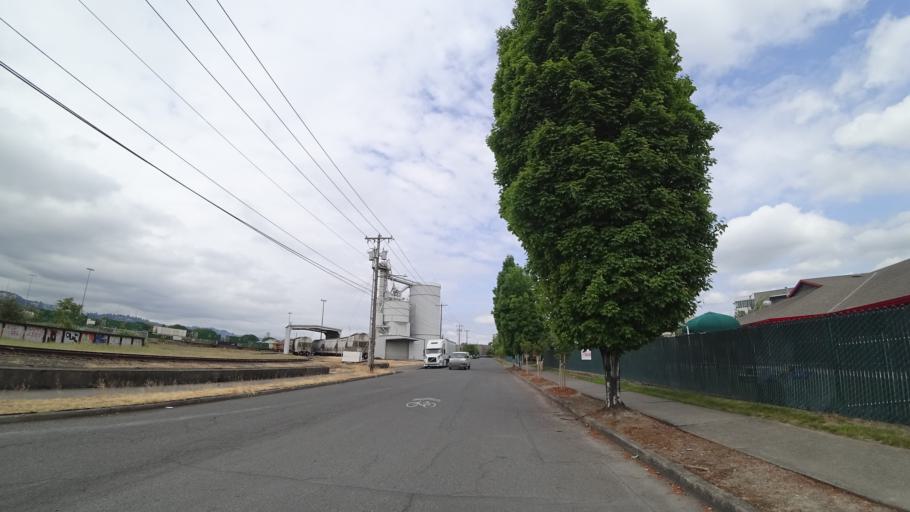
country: US
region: Oregon
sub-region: Multnomah County
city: Portland
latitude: 45.4935
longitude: -122.6428
